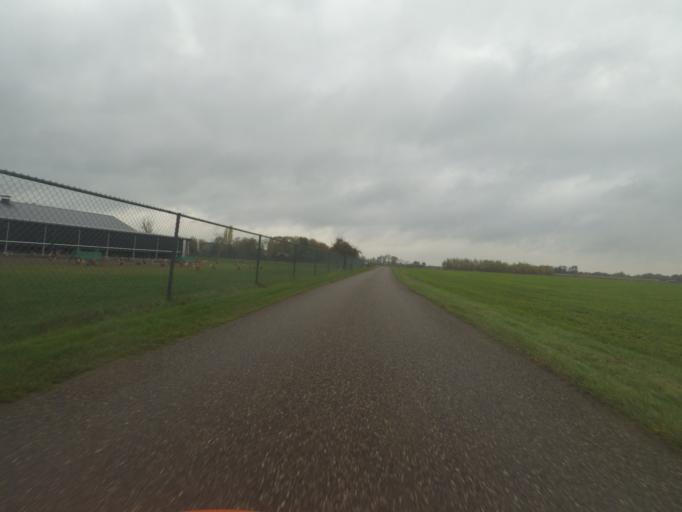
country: NL
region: Gelderland
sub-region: Gemeente Ede
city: Ederveen
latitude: 52.0829
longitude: 5.5667
